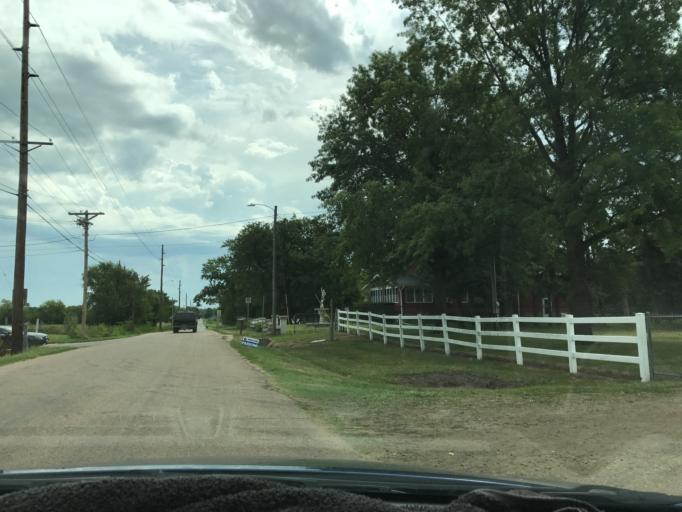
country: US
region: Nebraska
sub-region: Gage County
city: Beatrice
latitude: 40.2629
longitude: -96.7757
